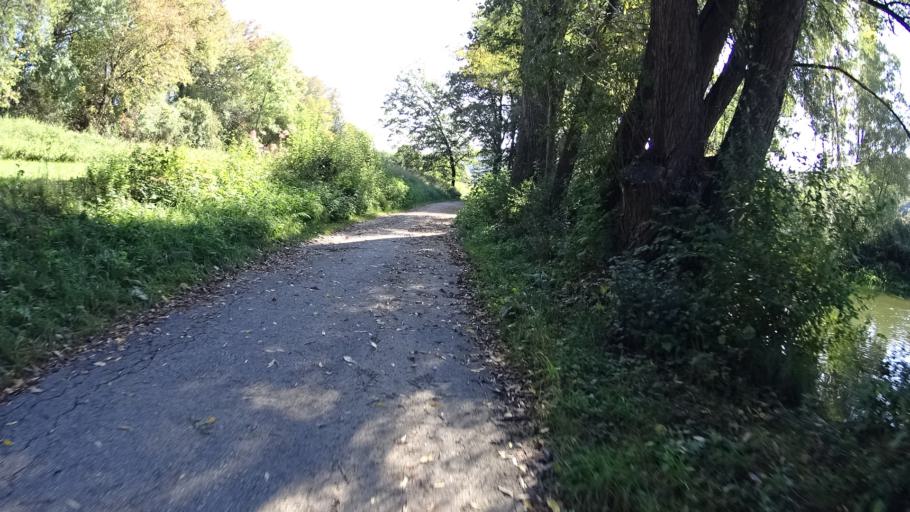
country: DE
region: Bavaria
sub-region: Upper Bavaria
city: Eichstaett
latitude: 48.8823
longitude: 11.2075
